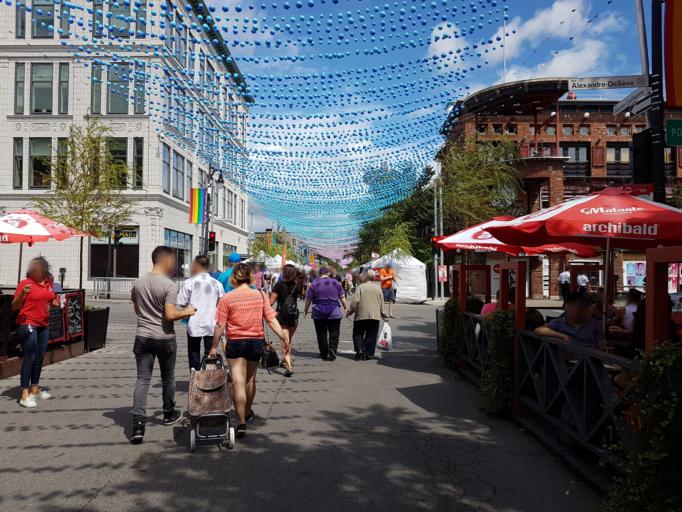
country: CA
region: Quebec
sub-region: Montreal
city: Montreal
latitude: 45.5210
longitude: -73.5539
